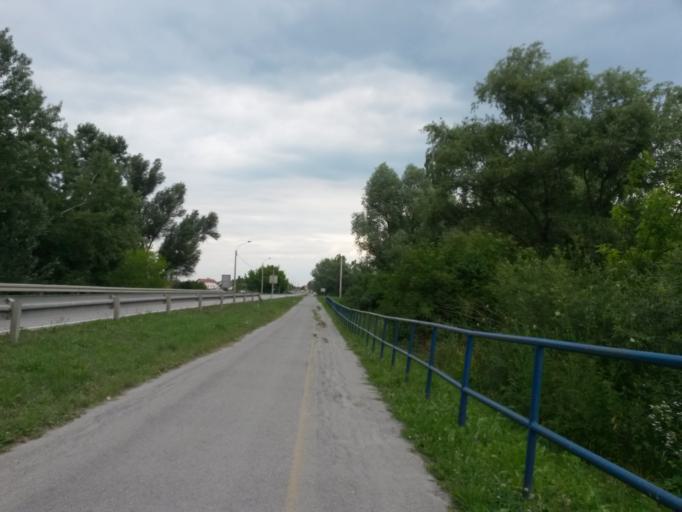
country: HR
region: Osjecko-Baranjska
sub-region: Grad Osijek
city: Bilje
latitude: 45.5913
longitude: 18.7367
